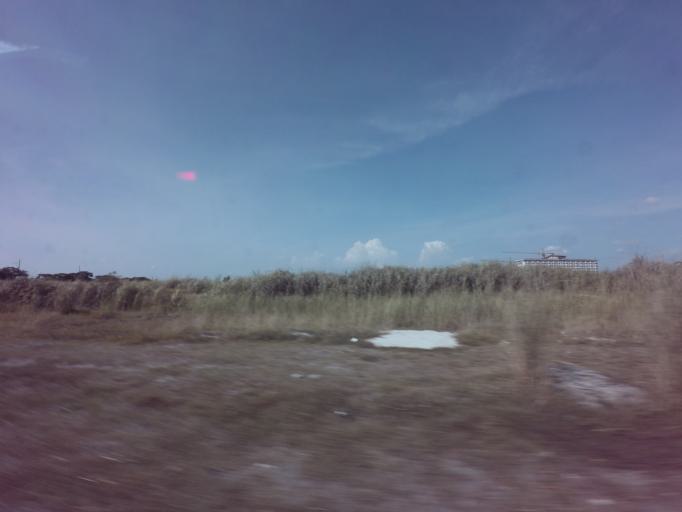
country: PH
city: Sambayanihan People's Village
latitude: 14.4779
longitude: 120.9868
